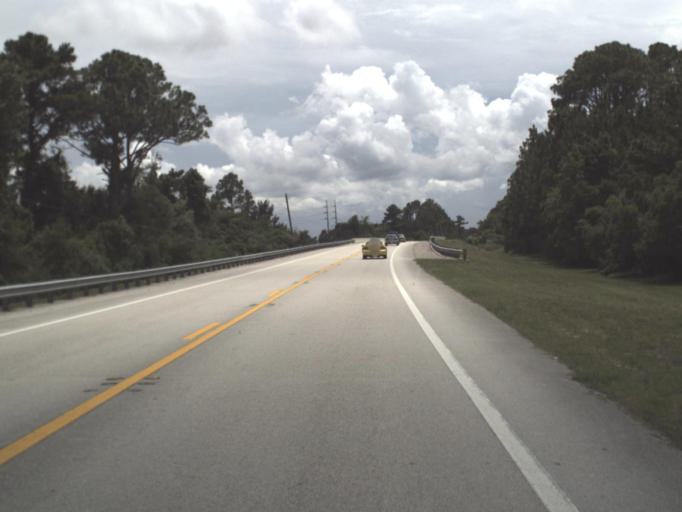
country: US
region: Florida
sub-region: Nassau County
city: Yulee
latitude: 30.5857
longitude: -81.6012
